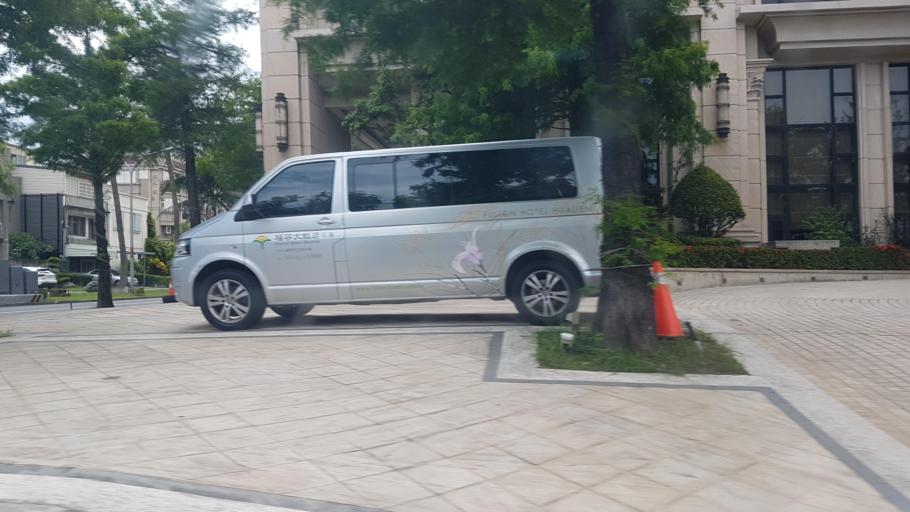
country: TW
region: Taiwan
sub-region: Hualien
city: Hualian
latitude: 23.9954
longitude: 121.6333
